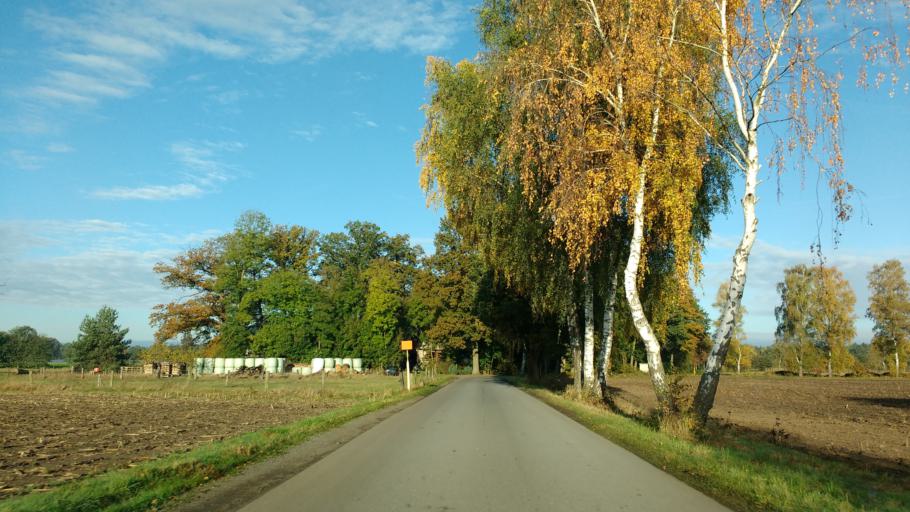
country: DE
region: North Rhine-Westphalia
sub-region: Regierungsbezirk Detmold
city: Hovelhof
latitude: 51.7677
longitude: 8.6853
